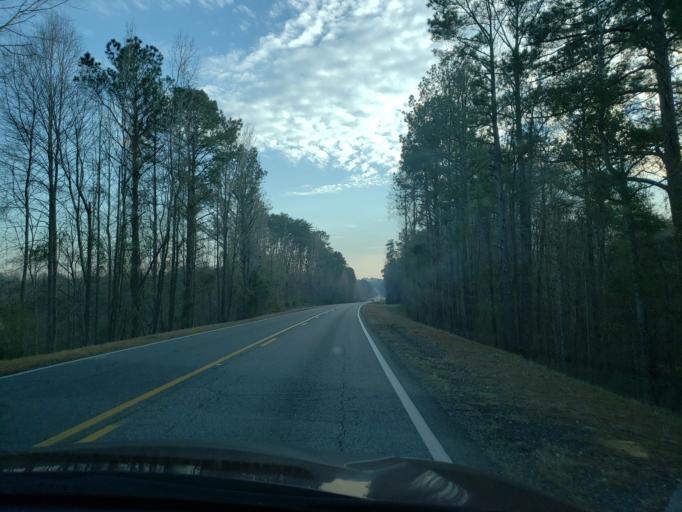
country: US
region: Alabama
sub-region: Hale County
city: Greensboro
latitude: 32.7303
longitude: -87.5877
